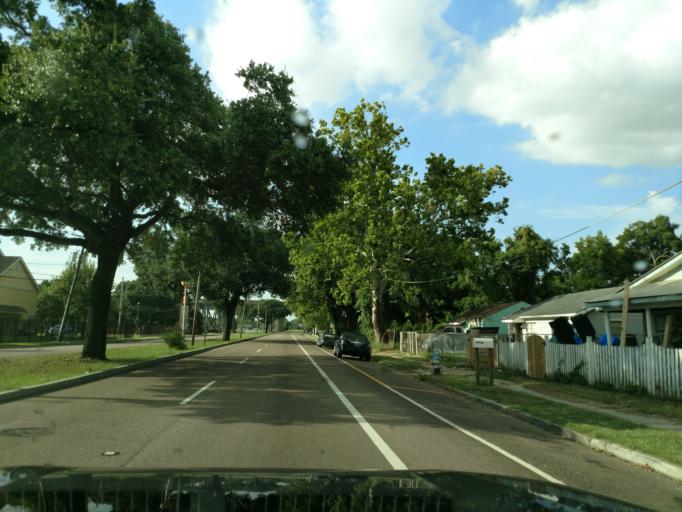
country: US
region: Louisiana
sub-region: Jefferson Parish
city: Gretna
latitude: 29.9355
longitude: -90.0414
